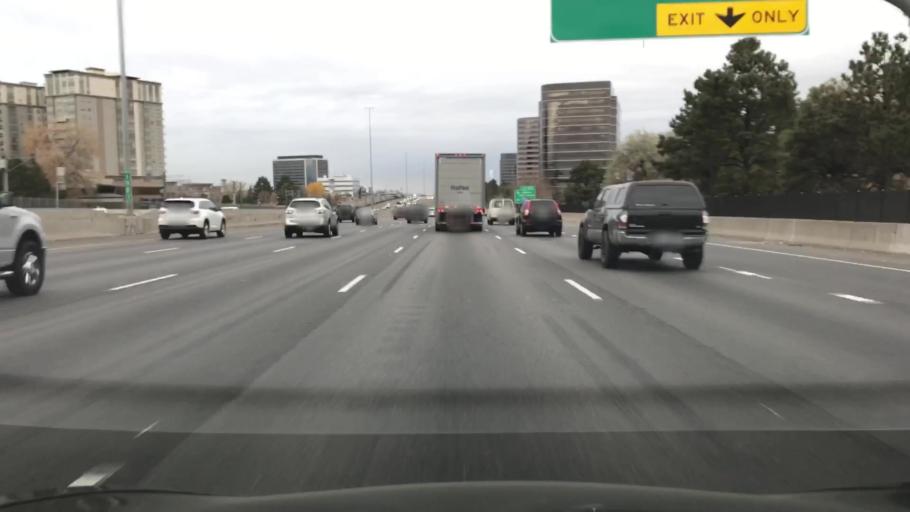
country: US
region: Colorado
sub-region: Arapahoe County
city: Castlewood
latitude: 39.6144
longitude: -104.8960
